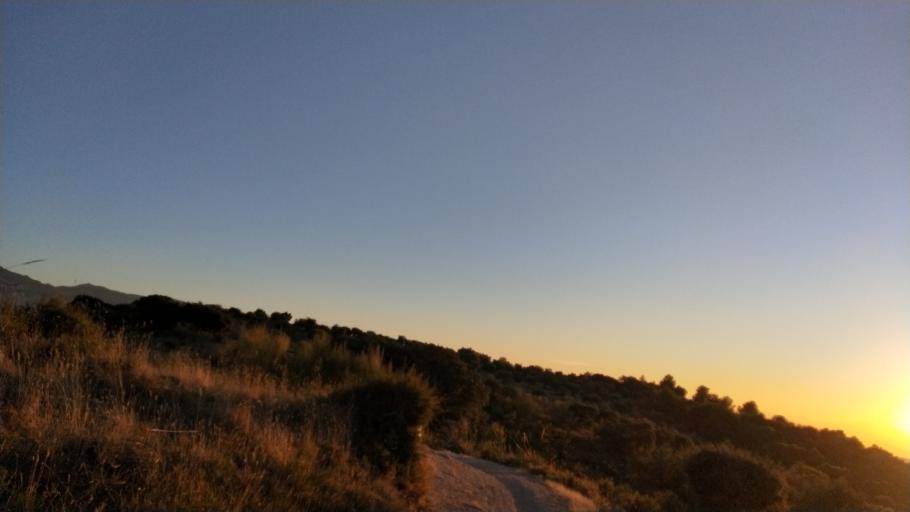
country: ES
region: Andalusia
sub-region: Provincia de Granada
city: Huetor Santillan
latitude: 37.2032
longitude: -3.5018
